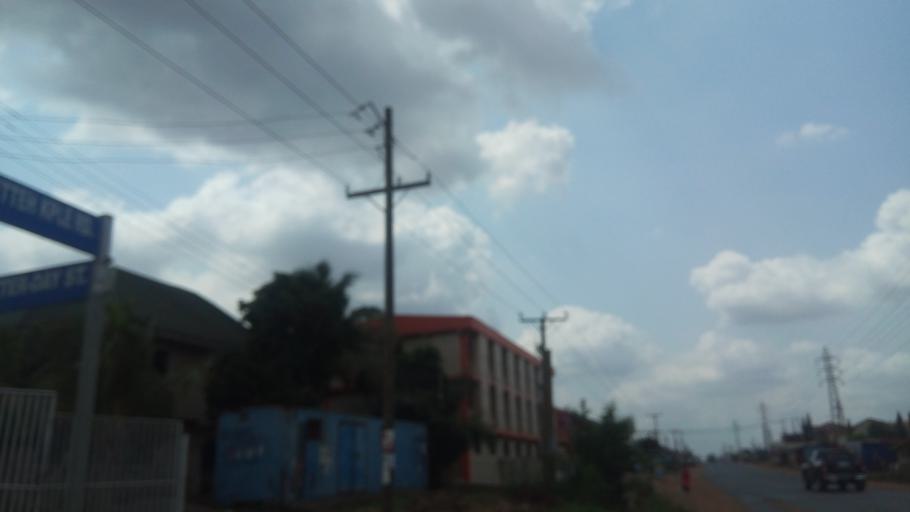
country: GH
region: Greater Accra
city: Tema
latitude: 5.7078
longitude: -0.0218
